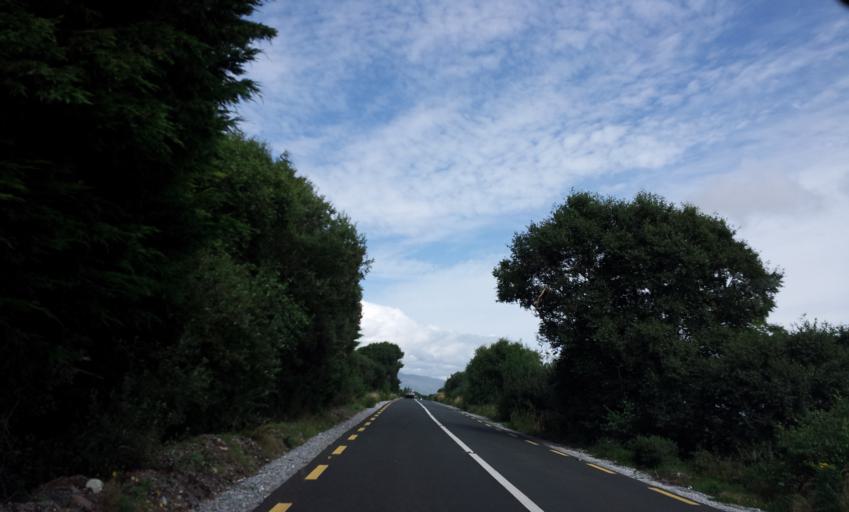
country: IE
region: Munster
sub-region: Ciarrai
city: Killorglin
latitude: 52.0763
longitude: -9.8789
